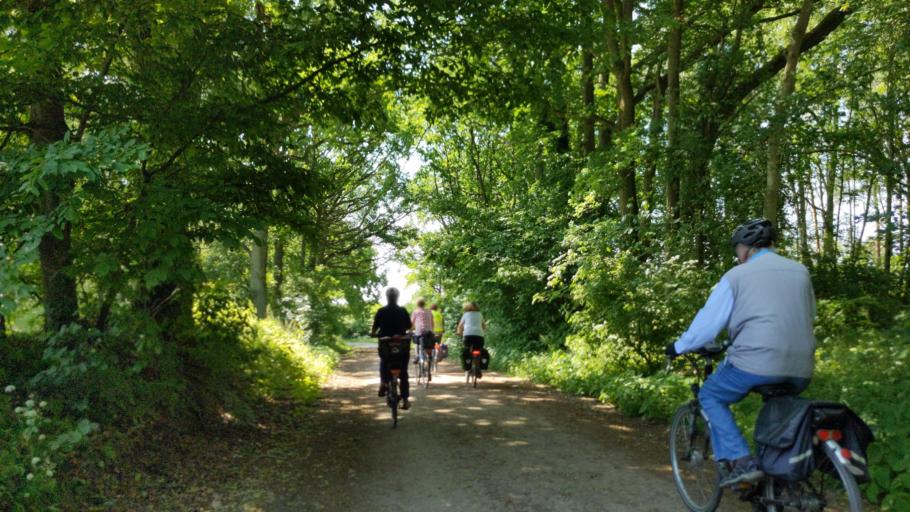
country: DE
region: Schleswig-Holstein
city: Klempau
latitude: 53.7666
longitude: 10.6523
